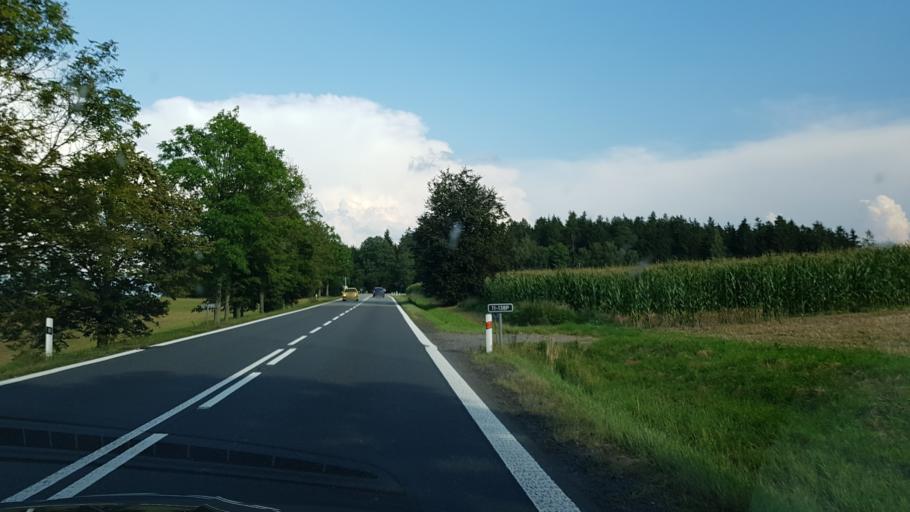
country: CZ
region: Pardubicky
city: Zamberk
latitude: 50.1113
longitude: 16.3822
